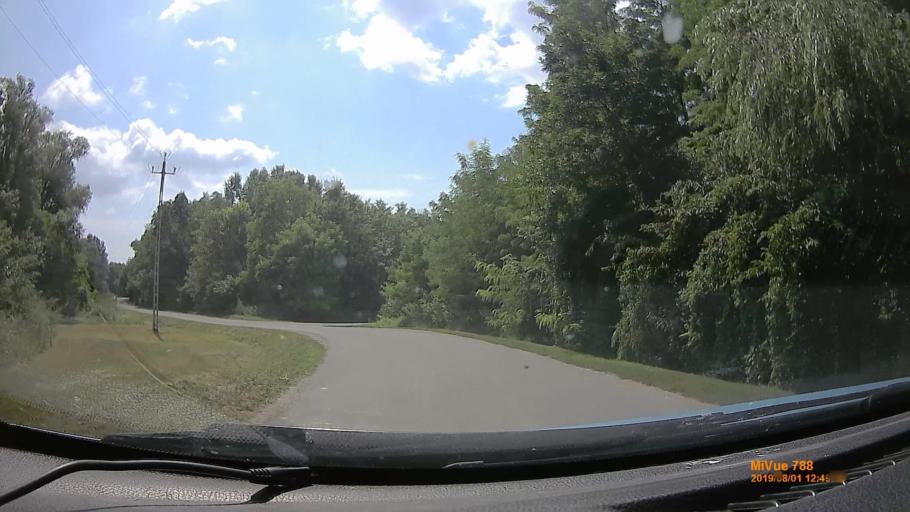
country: HR
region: Osjecko-Baranjska
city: Viljevo
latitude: 45.8133
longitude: 18.1036
